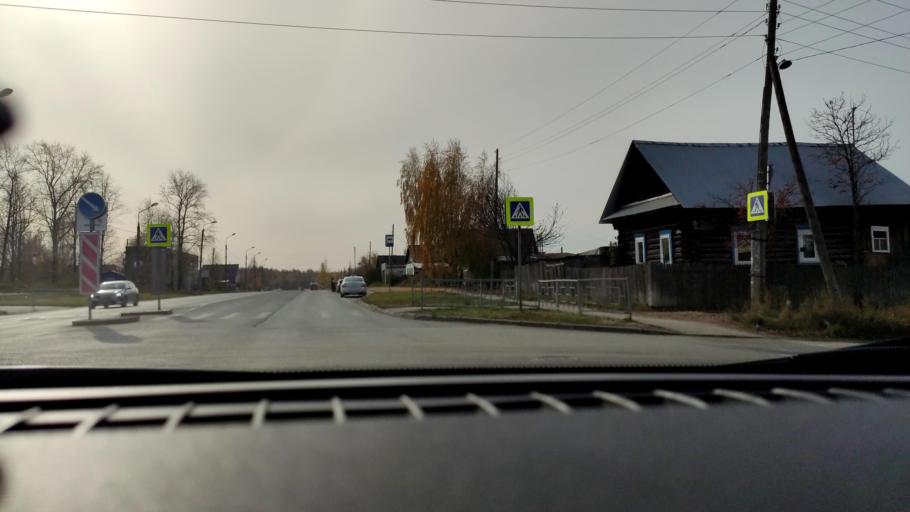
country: RU
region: Perm
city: Polazna
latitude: 58.1173
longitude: 56.4019
